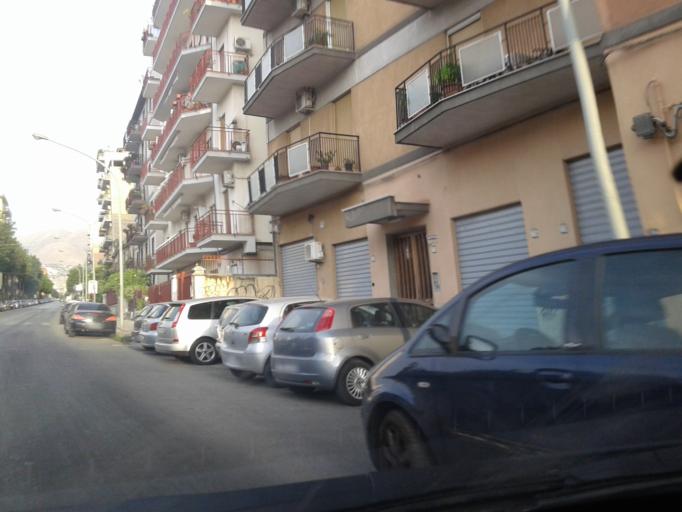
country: IT
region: Sicily
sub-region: Palermo
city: Palermo
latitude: 38.1105
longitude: 13.3370
